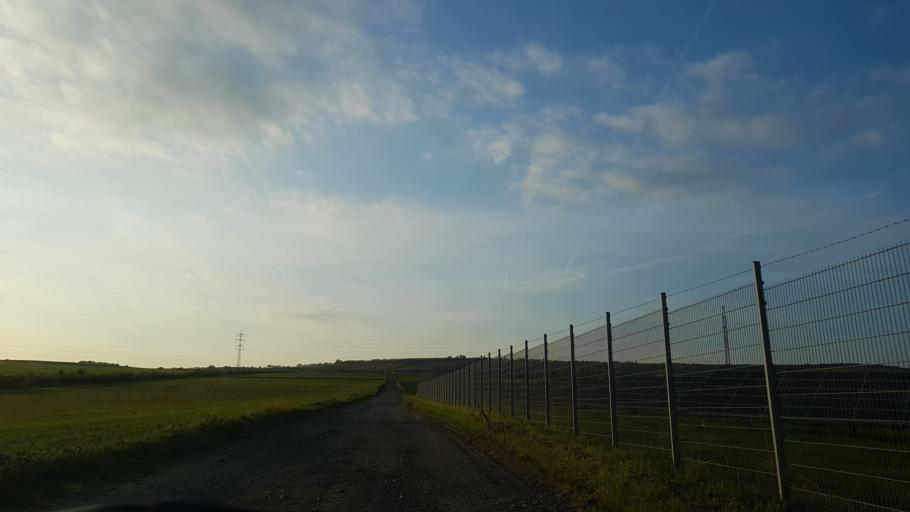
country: CZ
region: Zlin
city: Polesovice
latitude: 49.0198
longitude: 17.3483
